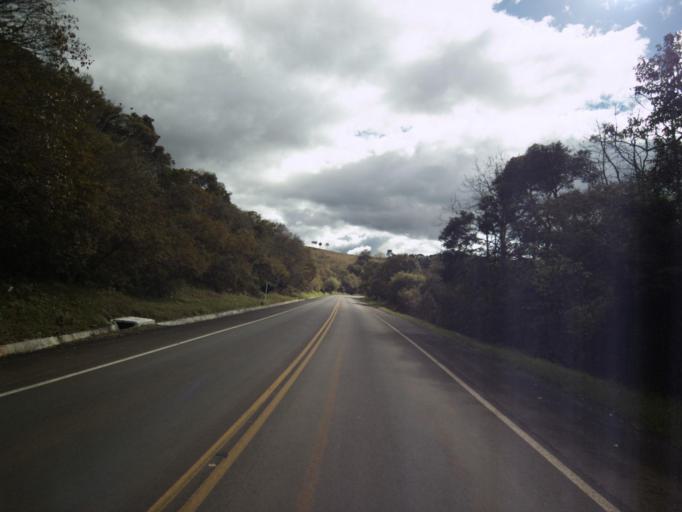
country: BR
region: Santa Catarina
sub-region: Concordia
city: Concordia
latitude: -27.3507
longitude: -51.9891
